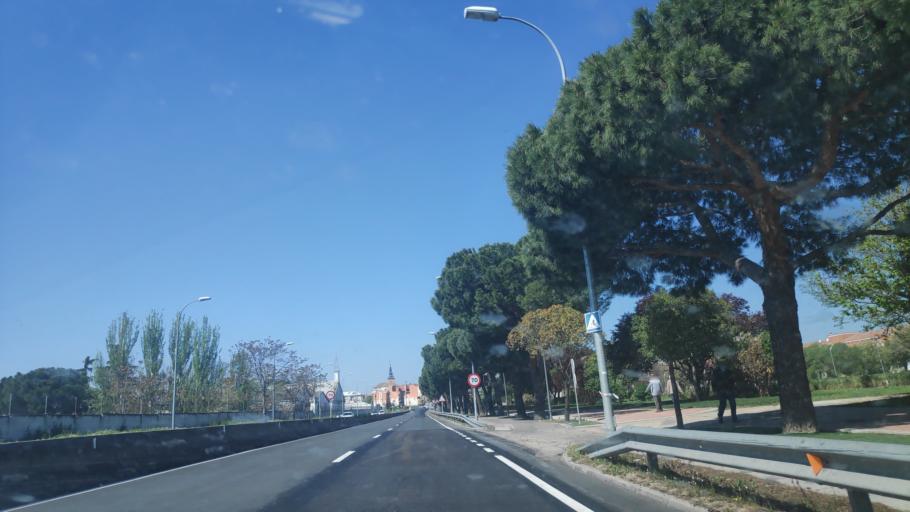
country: ES
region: Madrid
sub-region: Provincia de Madrid
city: Getafe
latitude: 40.3046
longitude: -3.7205
